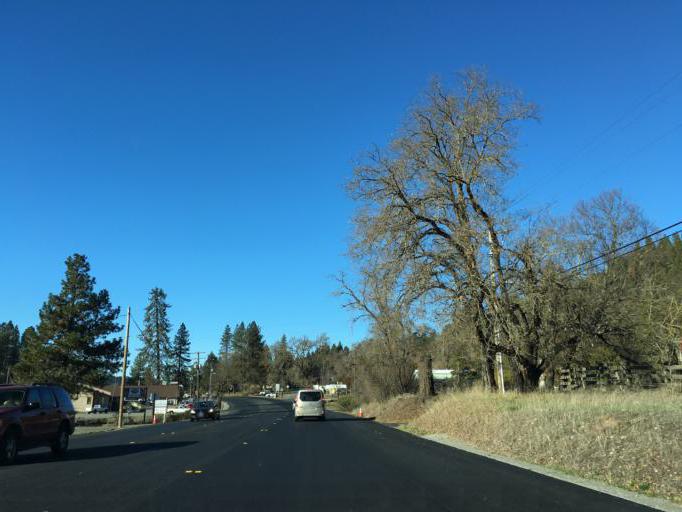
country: US
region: California
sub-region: Mendocino County
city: Laytonville
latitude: 39.6827
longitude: -123.4772
